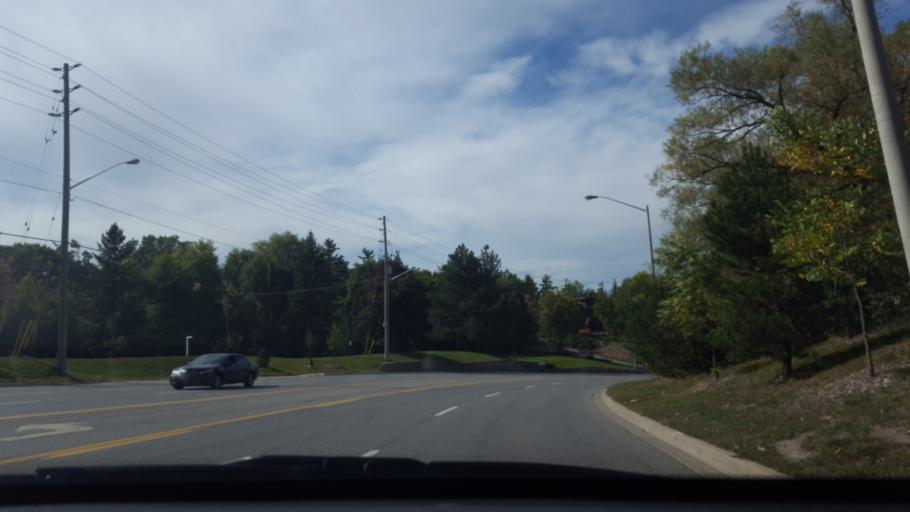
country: CA
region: Ontario
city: Vaughan
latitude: 43.8024
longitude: -79.5793
